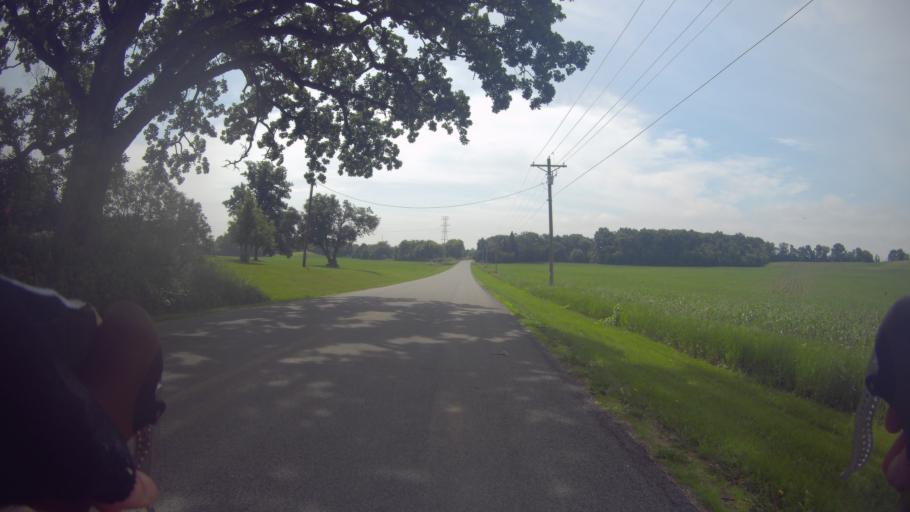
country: US
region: Wisconsin
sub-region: Rock County
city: Edgerton
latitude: 42.8639
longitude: -89.0507
